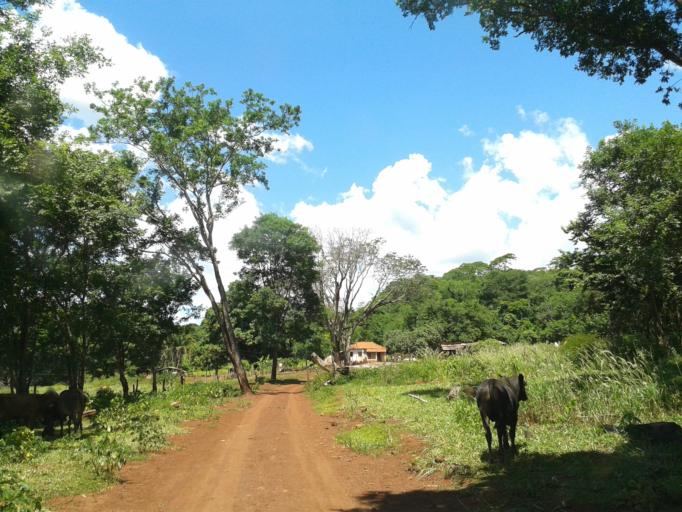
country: BR
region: Minas Gerais
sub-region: Centralina
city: Centralina
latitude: -18.6837
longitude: -49.1862
